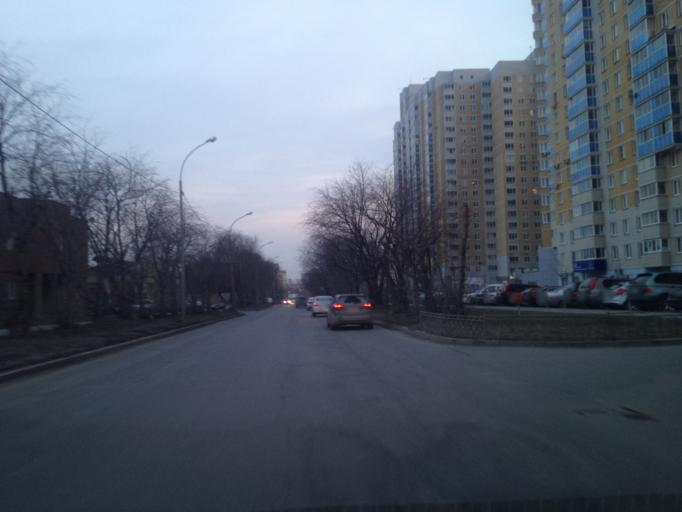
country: RU
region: Sverdlovsk
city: Yekaterinburg
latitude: 56.8346
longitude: 60.6620
